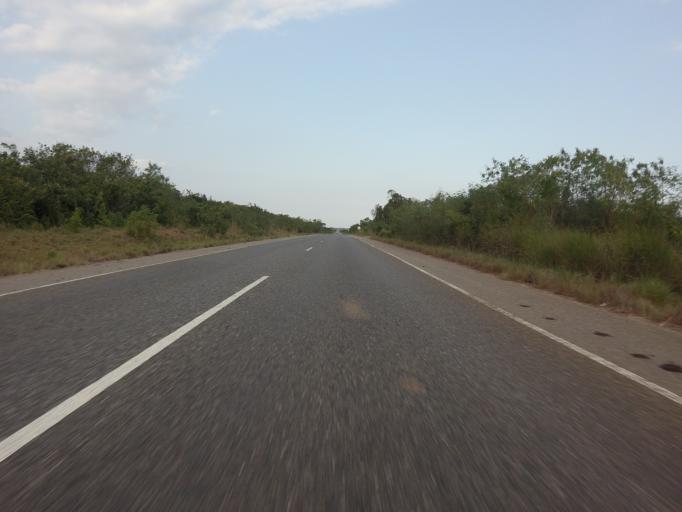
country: GH
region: Volta
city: Anloga
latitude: 6.0853
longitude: 0.5538
